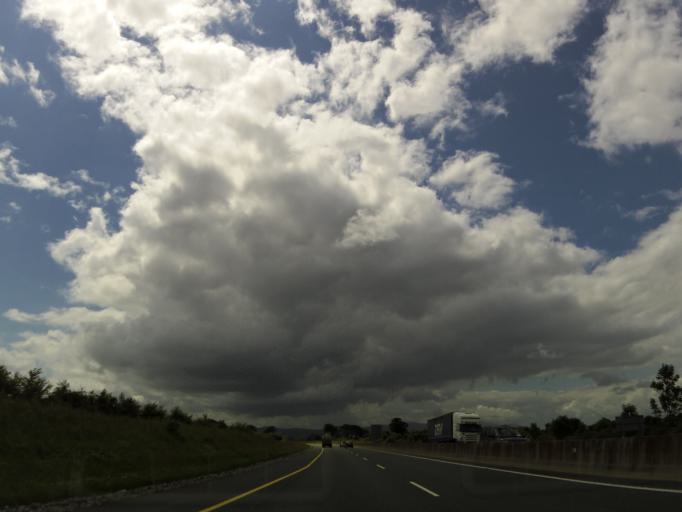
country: IE
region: Munster
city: Cashel
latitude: 52.4920
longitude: -7.8972
